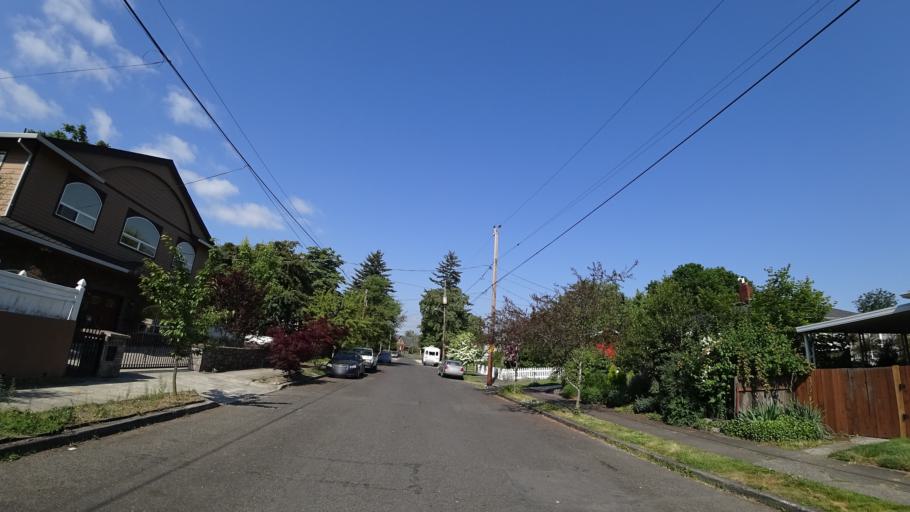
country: US
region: Oregon
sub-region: Multnomah County
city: Portland
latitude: 45.5691
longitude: -122.6503
